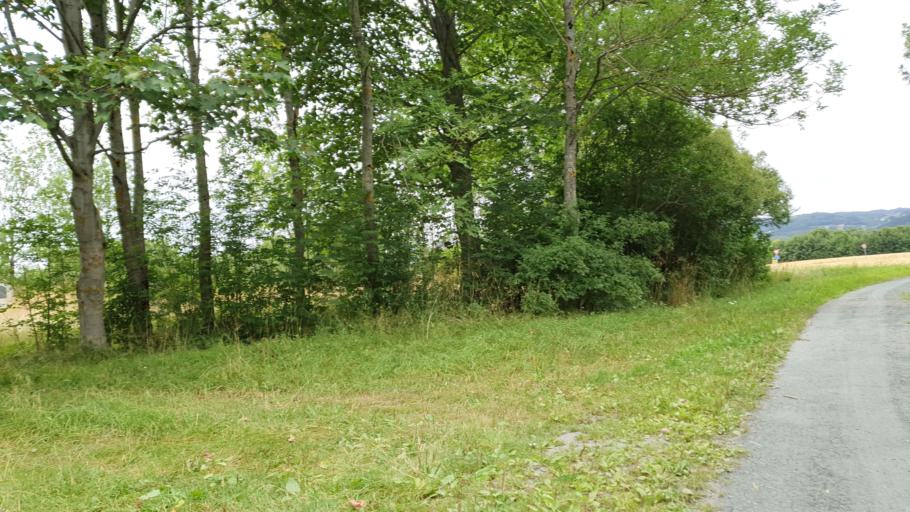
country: NO
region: Sor-Trondelag
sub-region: Rissa
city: Rissa
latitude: 63.4967
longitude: 10.0100
